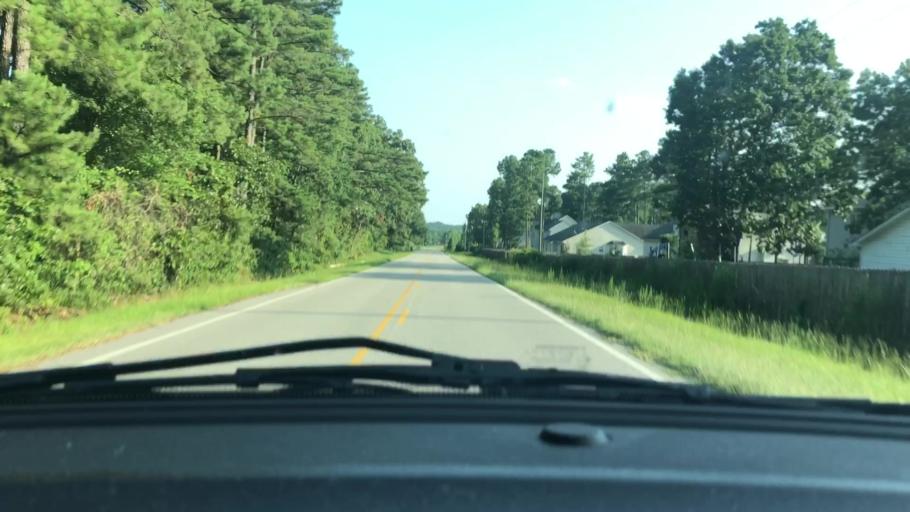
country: US
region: North Carolina
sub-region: Lee County
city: Broadway
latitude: 35.3433
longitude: -79.0725
